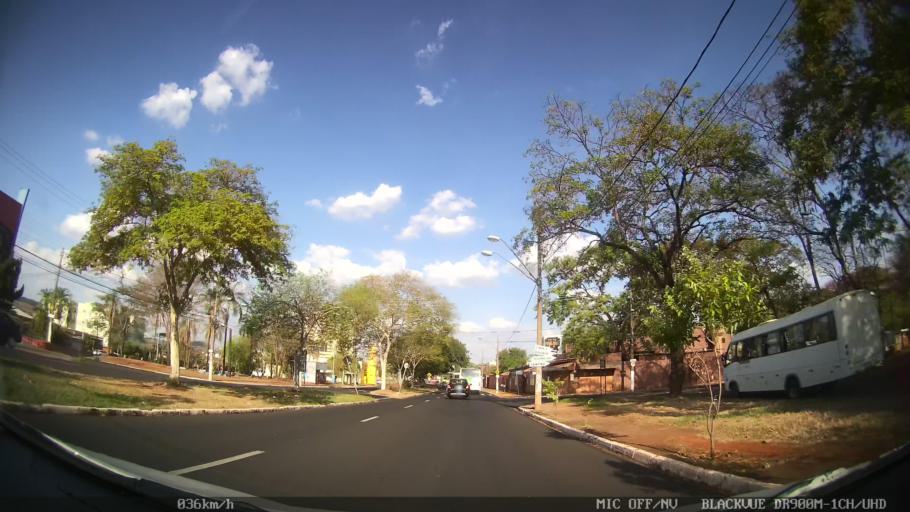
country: BR
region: Sao Paulo
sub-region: Ribeirao Preto
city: Ribeirao Preto
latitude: -21.1724
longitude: -47.7973
